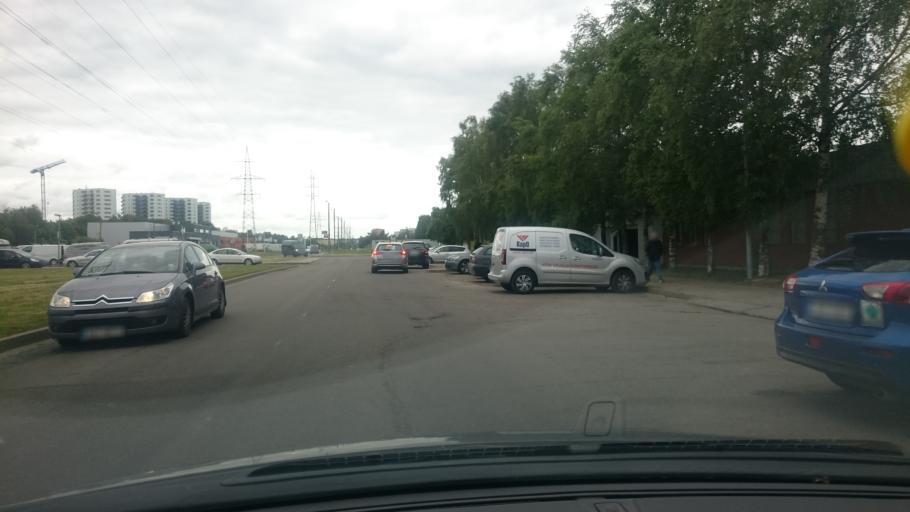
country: EE
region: Harju
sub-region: Saue vald
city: Laagri
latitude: 59.4126
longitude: 24.6576
